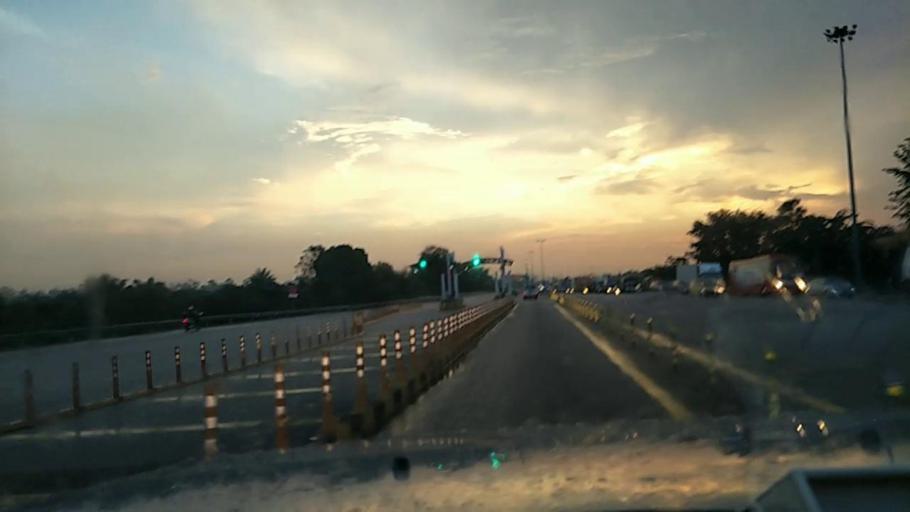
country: MY
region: Putrajaya
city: Putrajaya
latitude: 2.9250
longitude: 101.6125
